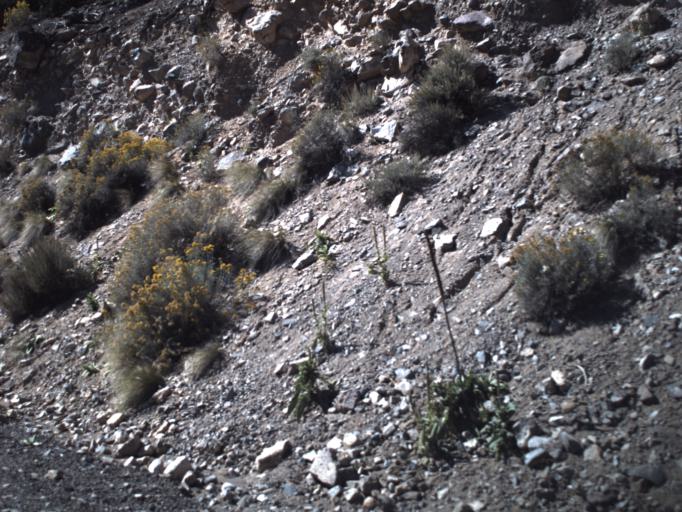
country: US
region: Utah
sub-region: Piute County
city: Junction
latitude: 38.2548
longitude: -112.3085
